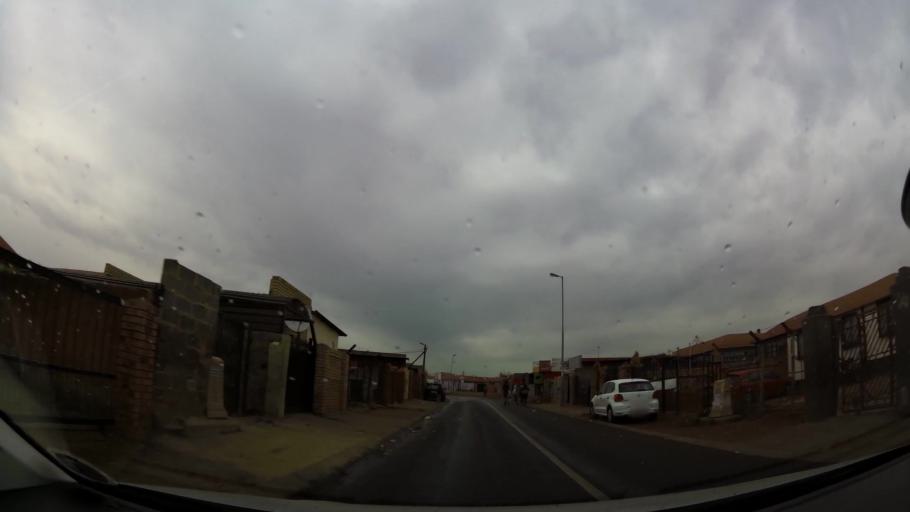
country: ZA
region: Gauteng
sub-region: City of Johannesburg Metropolitan Municipality
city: Soweto
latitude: -26.2479
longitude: 27.8759
